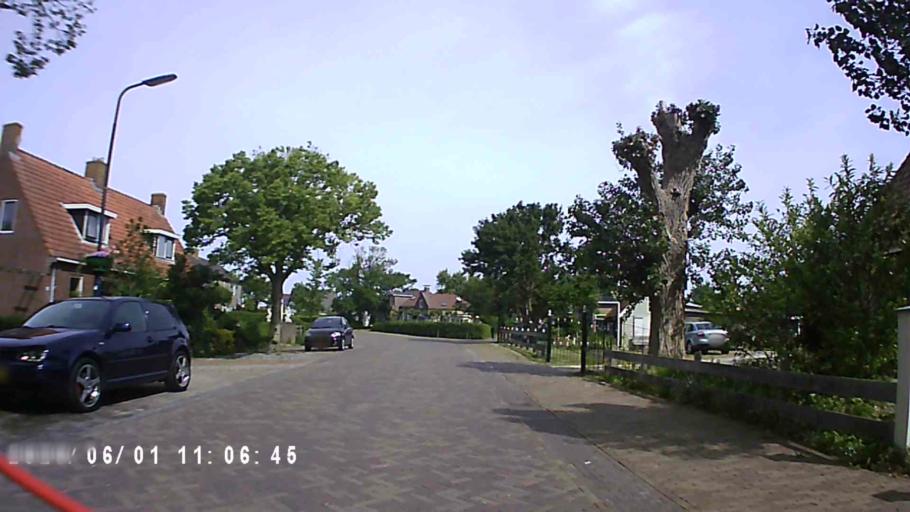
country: NL
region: Friesland
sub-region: Gemeente Franekeradeel
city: Sexbierum
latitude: 53.1959
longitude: 5.4605
